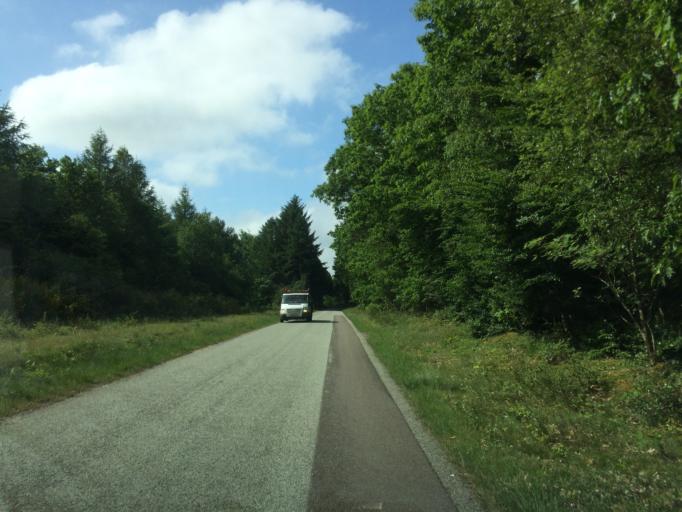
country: DK
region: Central Jutland
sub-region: Holstebro Kommune
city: Ulfborg
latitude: 56.2068
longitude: 8.4512
